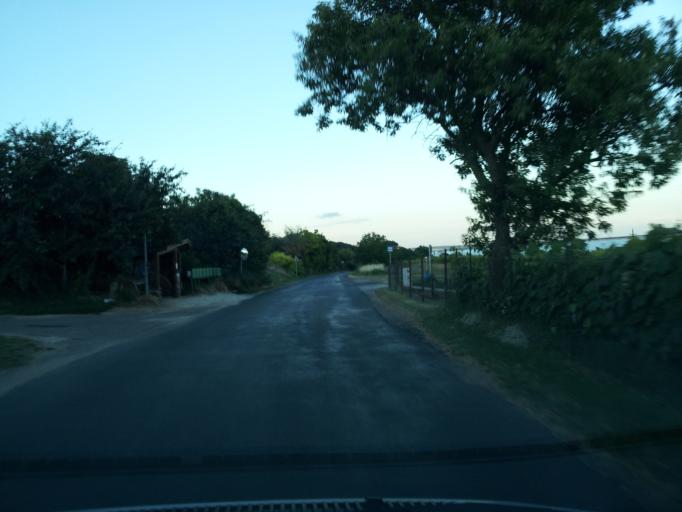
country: HU
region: Veszprem
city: Szentkiralyszabadja
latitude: 47.0153
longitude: 17.9791
